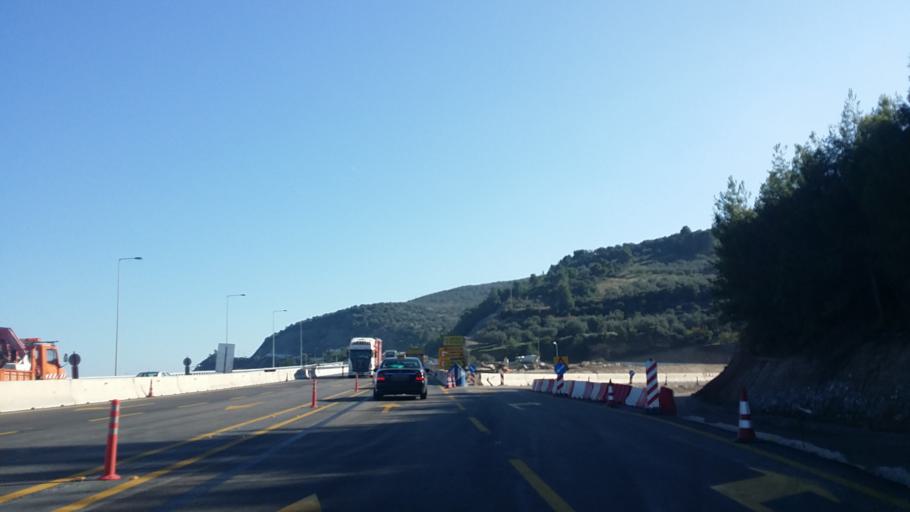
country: GR
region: West Greece
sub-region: Nomos Achaias
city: Akrata
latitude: 38.1765
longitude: 22.2374
